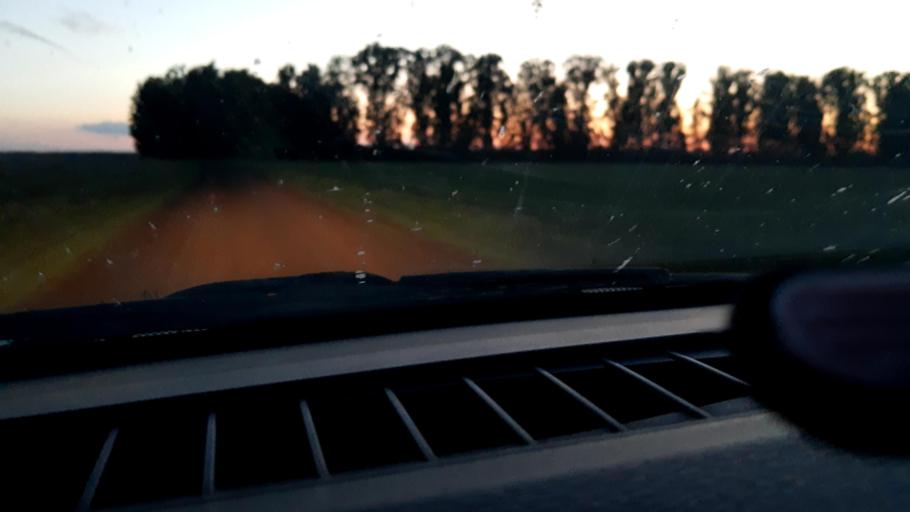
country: RU
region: Bashkortostan
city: Asanovo
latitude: 54.8635
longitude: 55.5759
